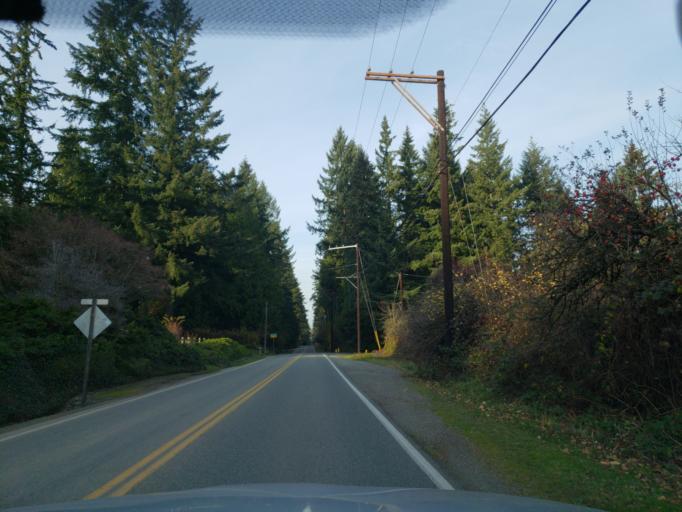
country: US
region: Washington
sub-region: Snohomish County
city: Maltby
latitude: 47.7806
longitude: -122.1322
